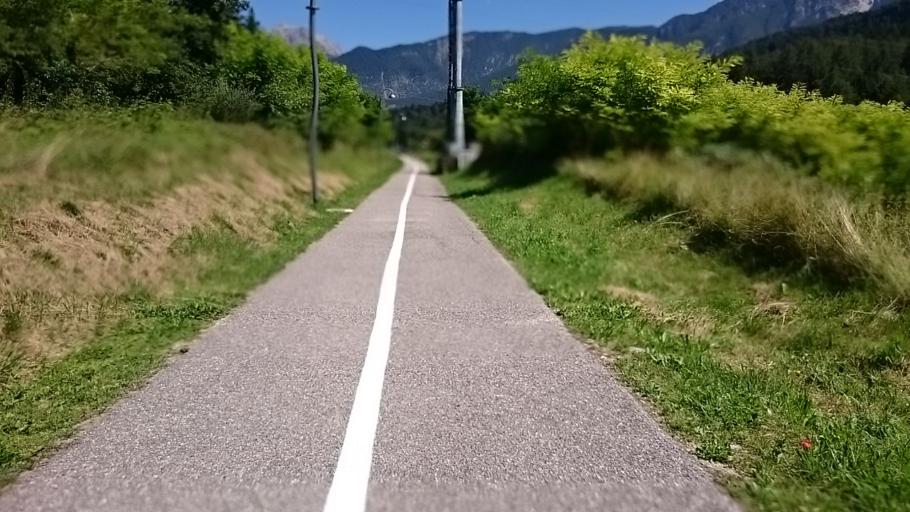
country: IT
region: Veneto
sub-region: Provincia di Belluno
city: Valle di Cadore
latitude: 46.4202
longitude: 12.3445
